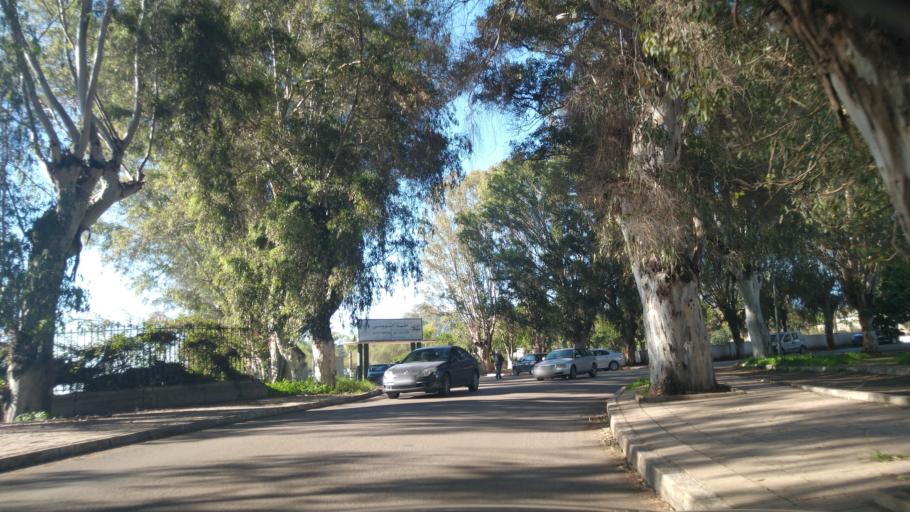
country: MA
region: Rabat-Sale-Zemmour-Zaer
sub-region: Rabat
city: Rabat
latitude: 33.9810
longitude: -6.8527
